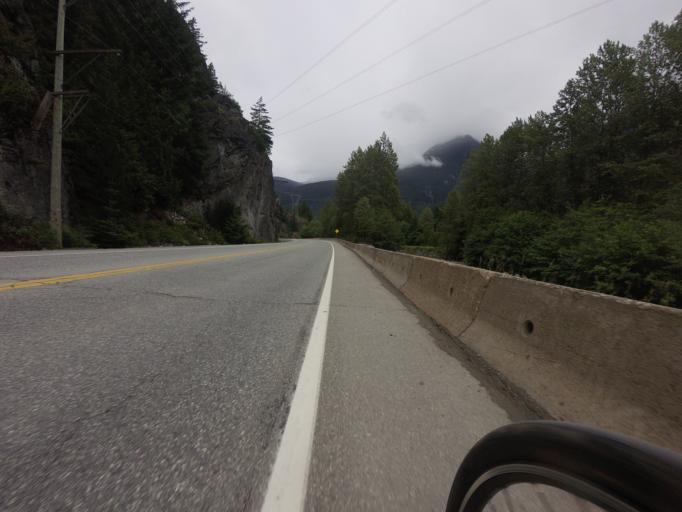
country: CA
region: British Columbia
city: Whistler
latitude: 50.1698
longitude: -122.8909
